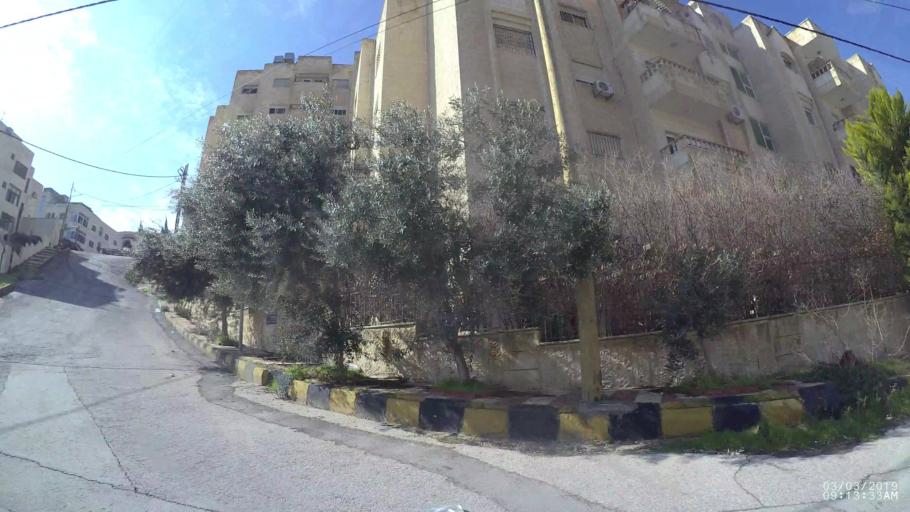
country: JO
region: Amman
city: Al Jubayhah
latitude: 32.0015
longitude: 35.8935
